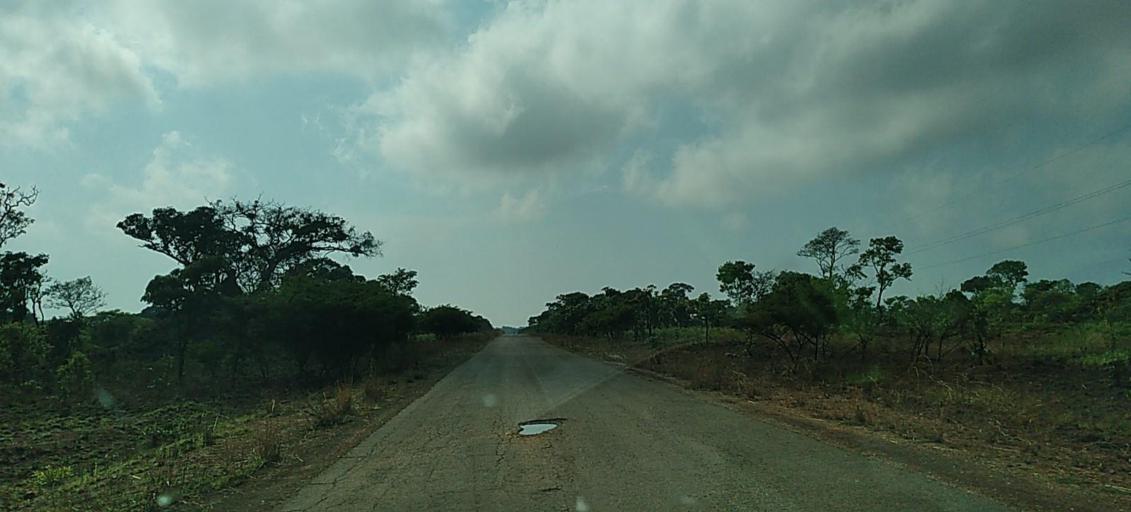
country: ZM
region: North-Western
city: Mwinilunga
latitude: -11.7649
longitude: 24.9998
